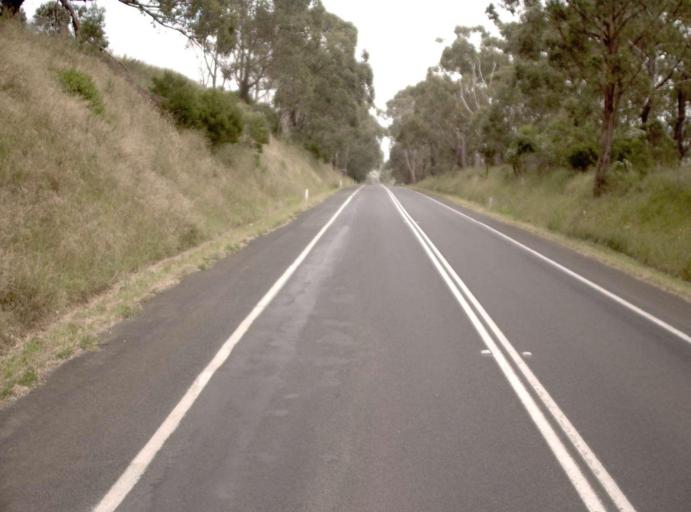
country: AU
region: Victoria
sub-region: Baw Baw
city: Warragul
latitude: -38.4067
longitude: 146.0651
